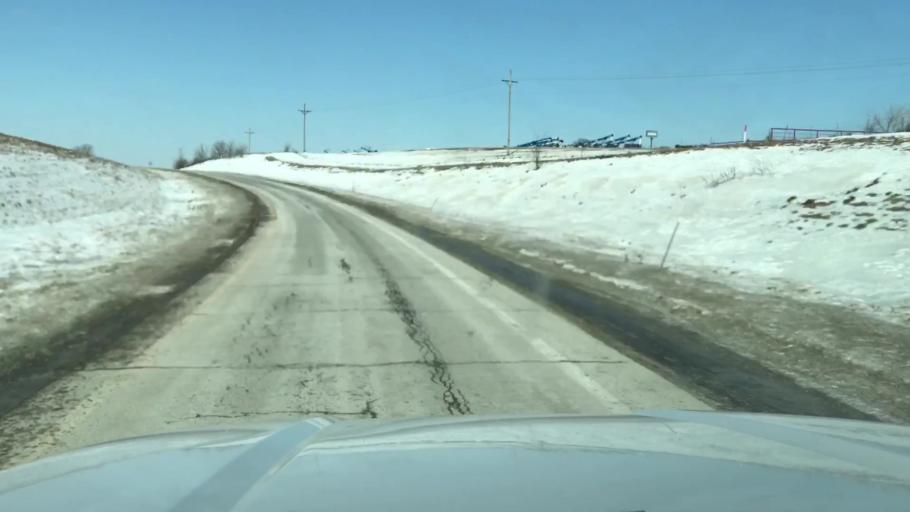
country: US
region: Missouri
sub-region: Andrew County
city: Savannah
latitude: 39.9623
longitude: -94.8612
